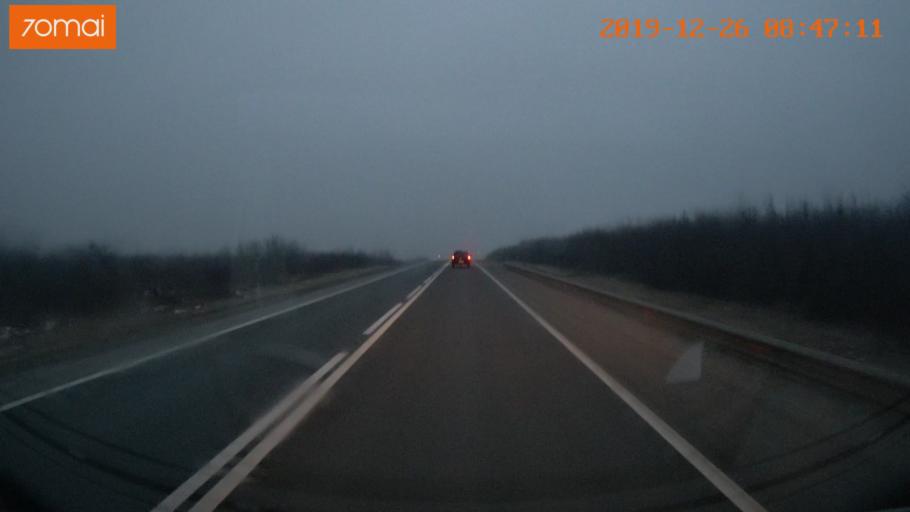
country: RU
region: Jaroslavl
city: Prechistoye
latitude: 58.6201
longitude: 40.3328
